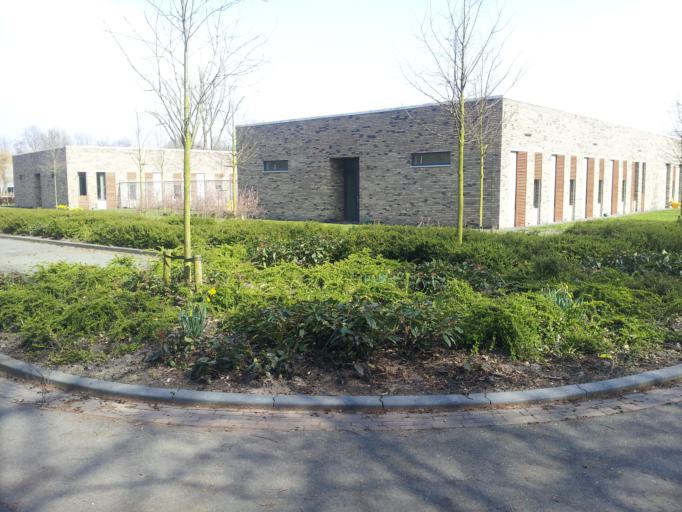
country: NL
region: South Holland
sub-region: Gemeente Wassenaar
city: Wassenaar
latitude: 52.0964
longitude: 4.4091
